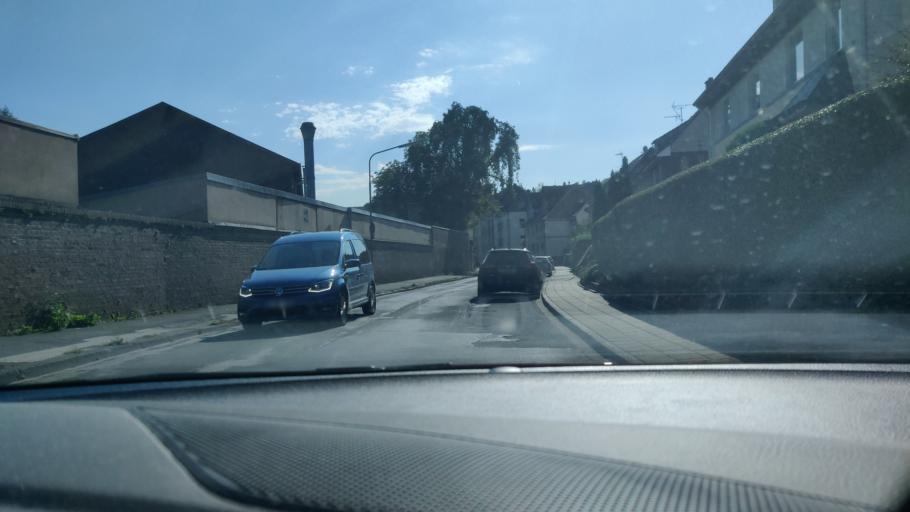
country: DE
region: North Rhine-Westphalia
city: Hattingen
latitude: 51.3603
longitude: 7.1221
